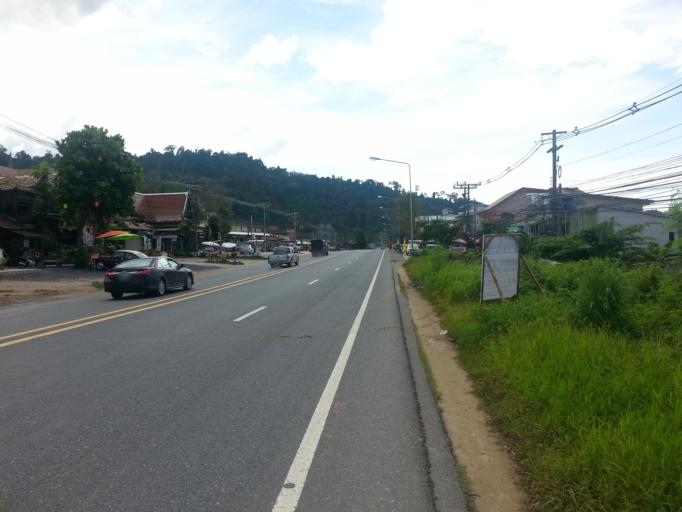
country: TH
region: Phangnga
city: Ban Khao Lak
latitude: 8.6484
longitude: 98.2522
